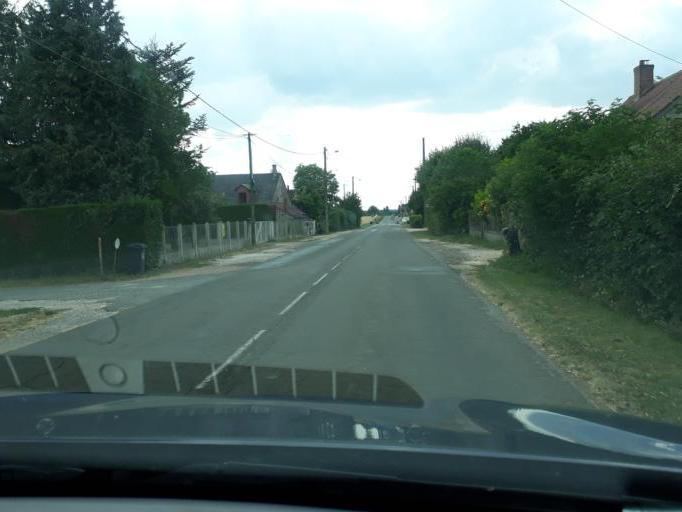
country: FR
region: Centre
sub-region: Departement du Cher
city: Baugy
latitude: 47.0932
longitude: 2.6858
